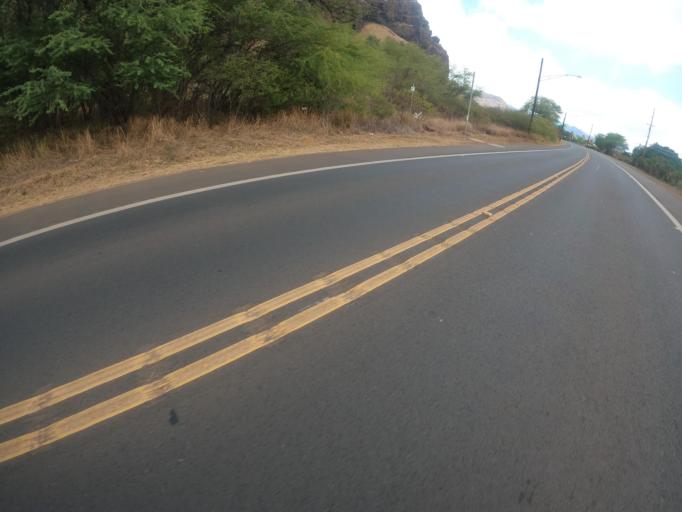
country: US
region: Hawaii
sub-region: Honolulu County
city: Makaha
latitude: 21.4815
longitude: -158.2274
